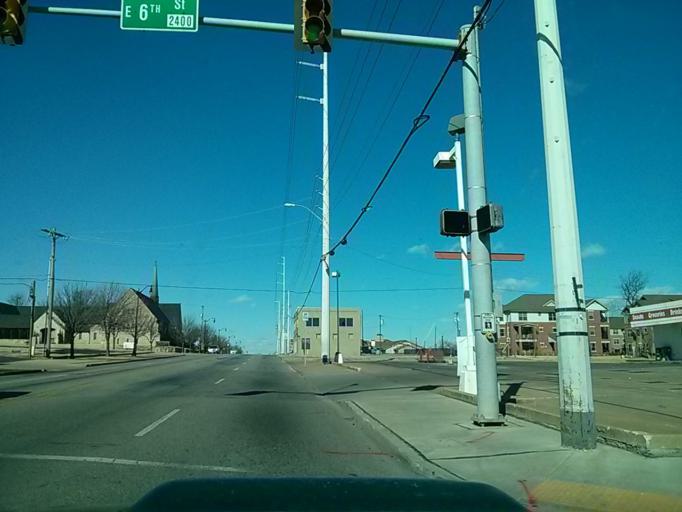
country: US
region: Oklahoma
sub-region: Tulsa County
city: Tulsa
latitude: 36.1518
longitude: -95.9581
